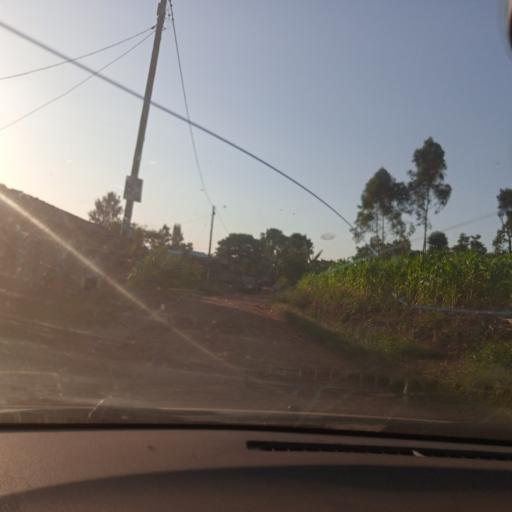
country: UG
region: Central Region
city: Masaka
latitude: -0.3313
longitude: 31.7546
